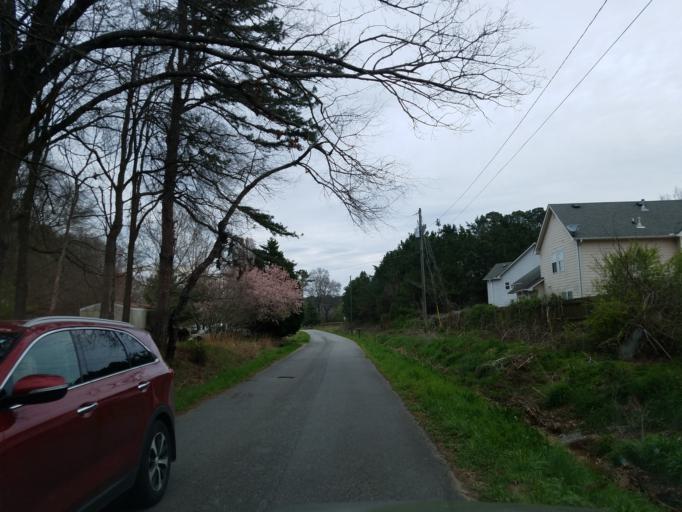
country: US
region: Georgia
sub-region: Bartow County
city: Cartersville
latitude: 34.2145
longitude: -84.7921
